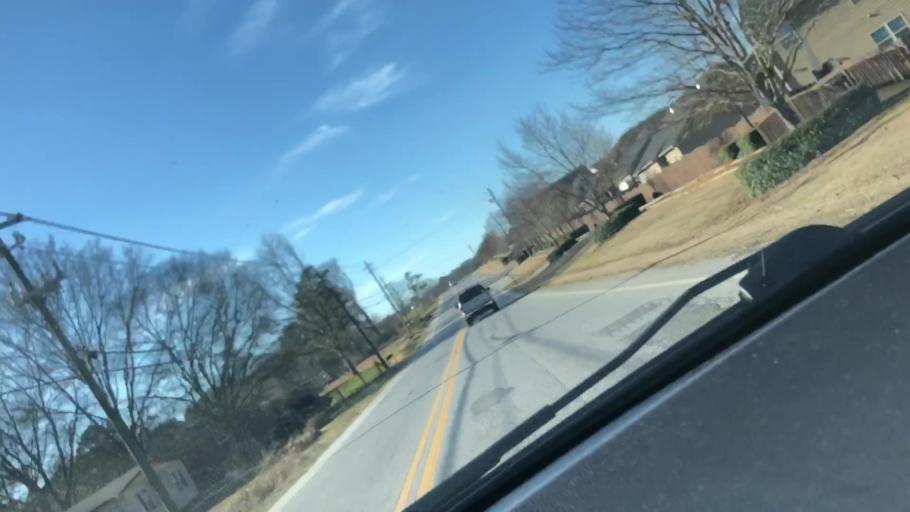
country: US
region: Georgia
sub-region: Bartow County
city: Cartersville
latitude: 34.2228
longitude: -84.8108
